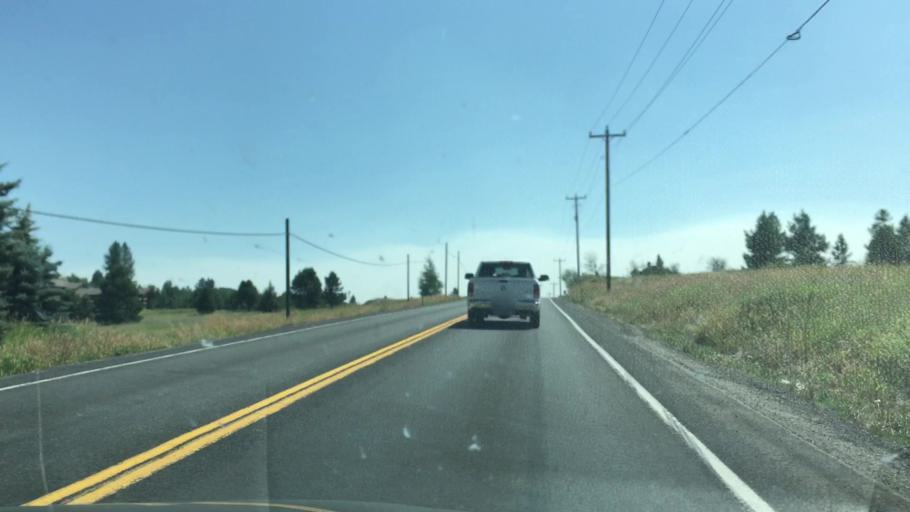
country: US
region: Idaho
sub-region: Valley County
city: McCall
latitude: 44.8818
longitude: -116.0907
